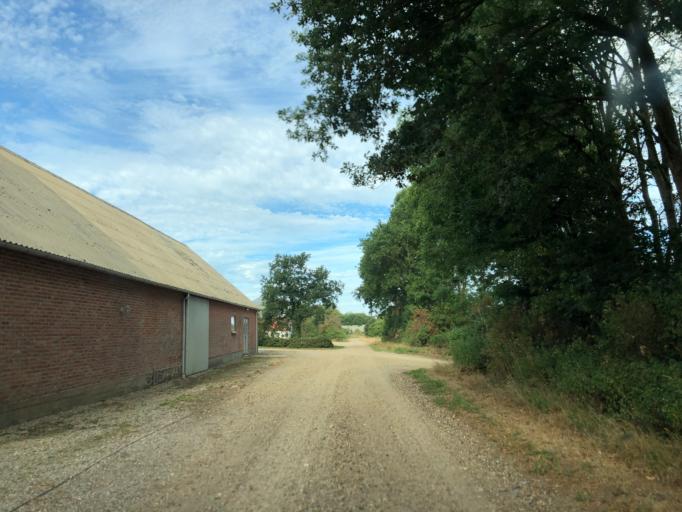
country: DK
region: Central Jutland
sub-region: Ringkobing-Skjern Kommune
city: Skjern
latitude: 56.0407
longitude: 8.4319
